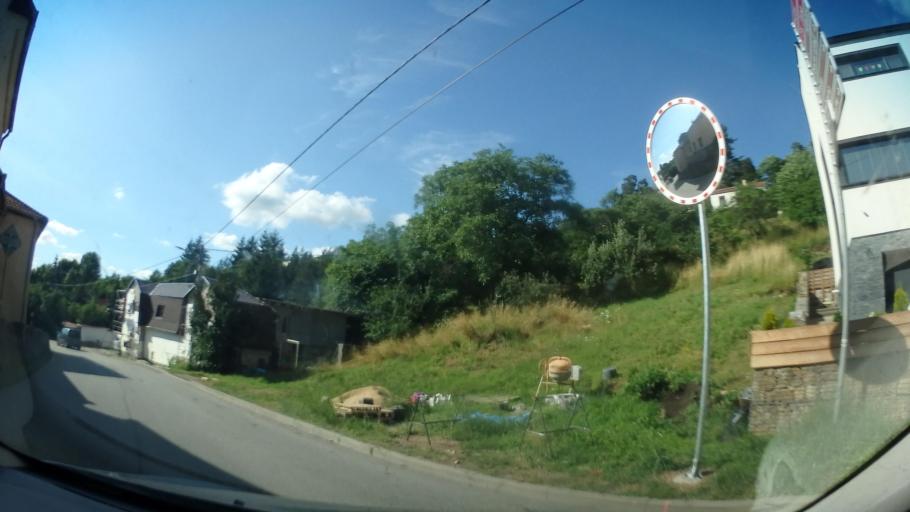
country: CZ
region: South Moravian
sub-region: Okres Blansko
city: Adamov
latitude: 49.3103
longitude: 16.6145
